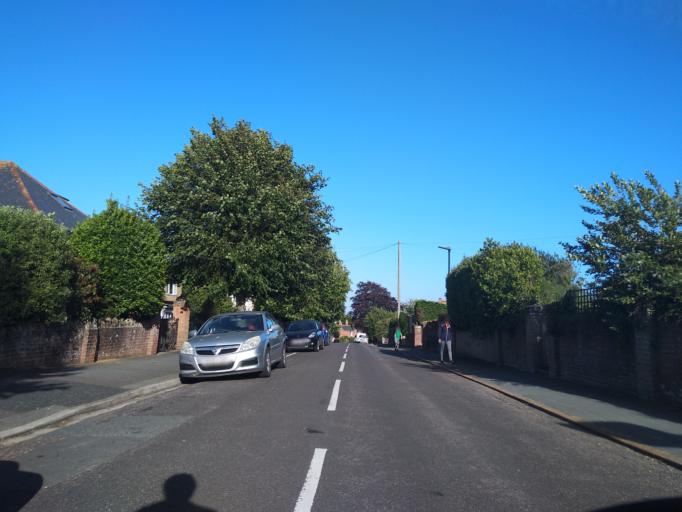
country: GB
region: England
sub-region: Isle of Wight
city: Sandown
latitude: 50.6584
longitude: -1.1545
